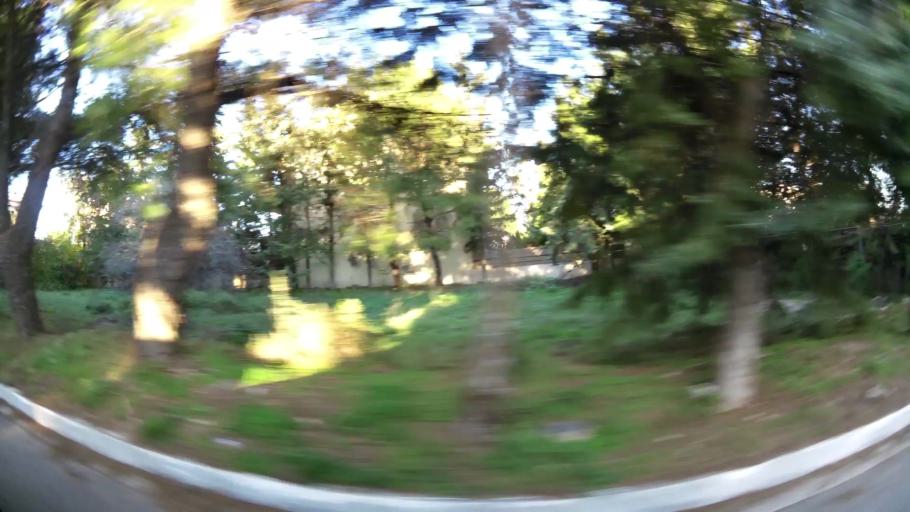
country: GR
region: Attica
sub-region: Nomarchia Anatolikis Attikis
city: Kryoneri
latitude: 38.1371
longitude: 23.8237
